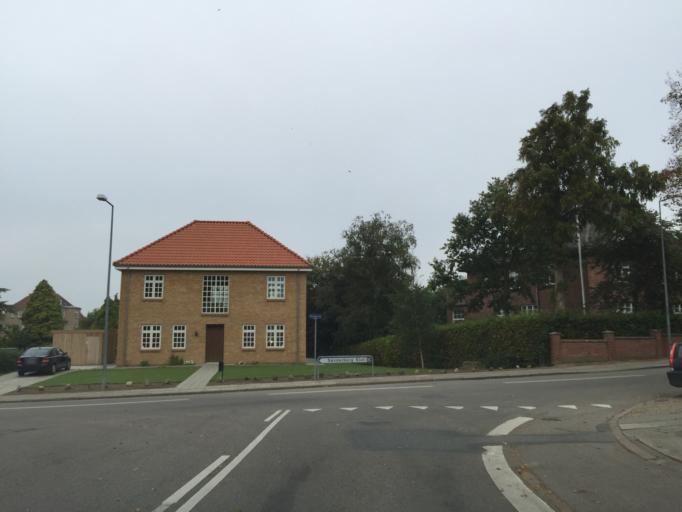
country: DK
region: South Denmark
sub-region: Sonderborg Kommune
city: Sonderborg
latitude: 54.9036
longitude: 9.7921
